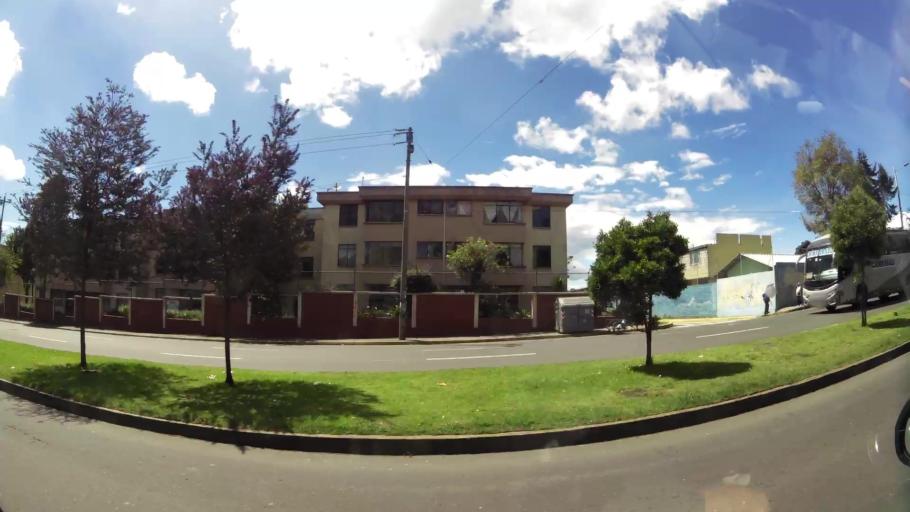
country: EC
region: Pichincha
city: Quito
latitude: -0.3036
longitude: -78.5591
